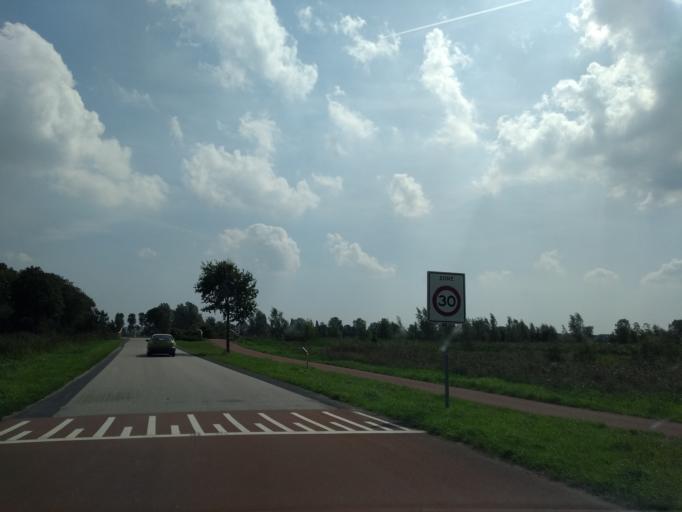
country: NL
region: Friesland
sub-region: Sudwest Fryslan
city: Oppenhuizen
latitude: 53.0342
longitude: 5.7190
